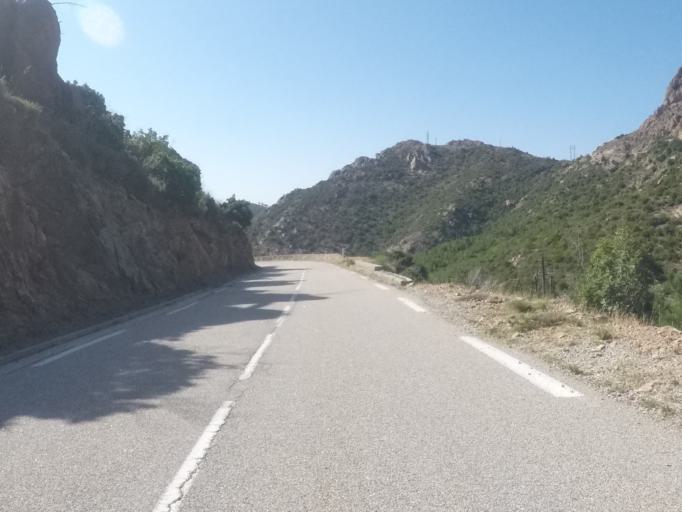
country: FR
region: Corsica
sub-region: Departement de la Corse-du-Sud
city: Zonza
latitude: 41.7700
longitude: 9.0457
